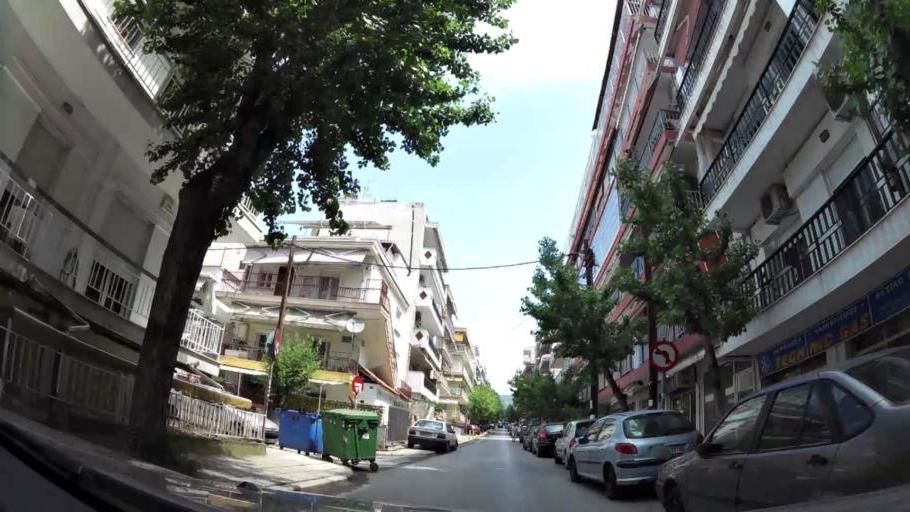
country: GR
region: Central Macedonia
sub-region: Nomos Thessalonikis
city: Triandria
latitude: 40.6162
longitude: 22.9786
